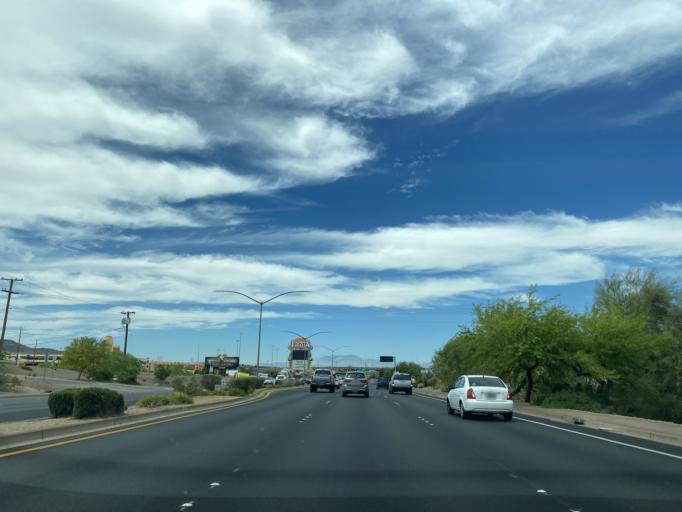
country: US
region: Nevada
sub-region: Clark County
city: Henderson
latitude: 36.0348
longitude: -115.0043
